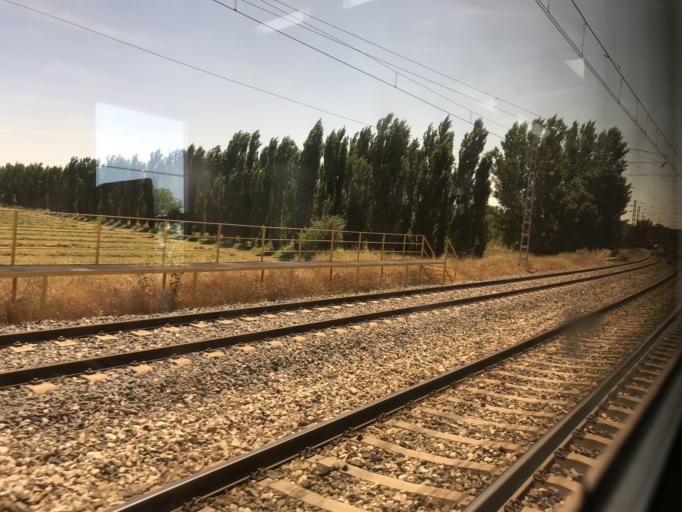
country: ES
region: Madrid
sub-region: Provincia de Madrid
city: Aranjuez
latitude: 40.0408
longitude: -3.6207
